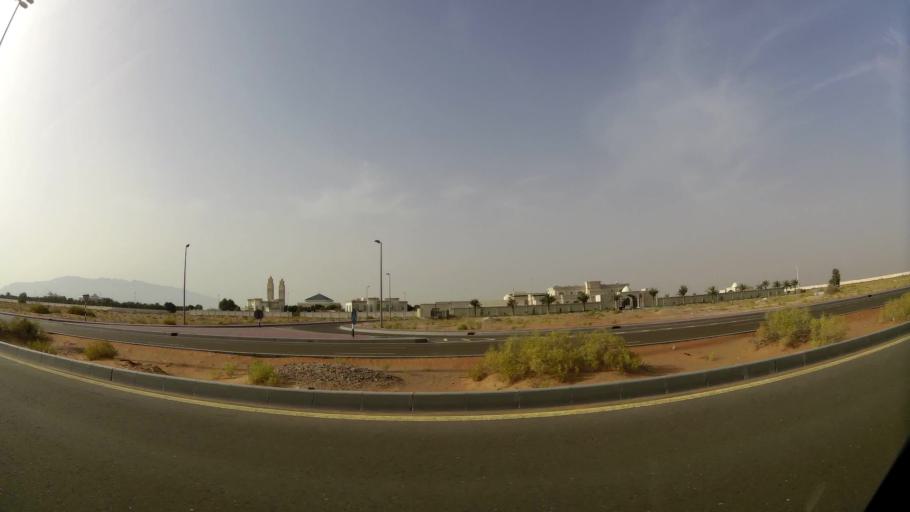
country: AE
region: Abu Dhabi
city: Al Ain
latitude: 24.1261
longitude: 55.6681
